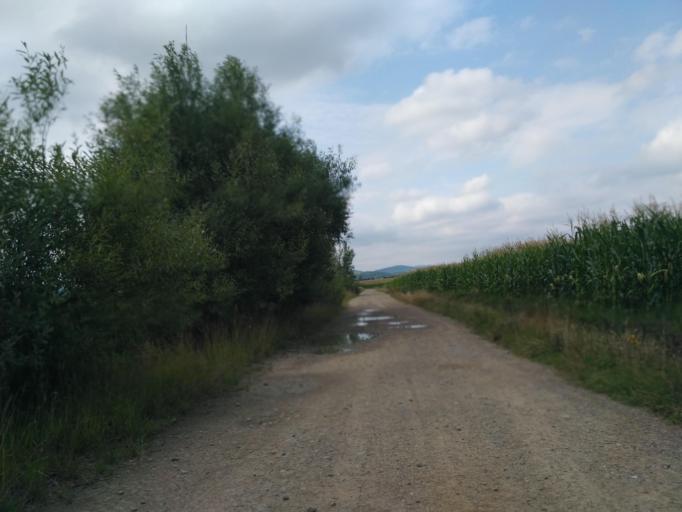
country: PL
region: Subcarpathian Voivodeship
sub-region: Powiat krosnienski
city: Rymanow
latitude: 49.6132
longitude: 21.8461
